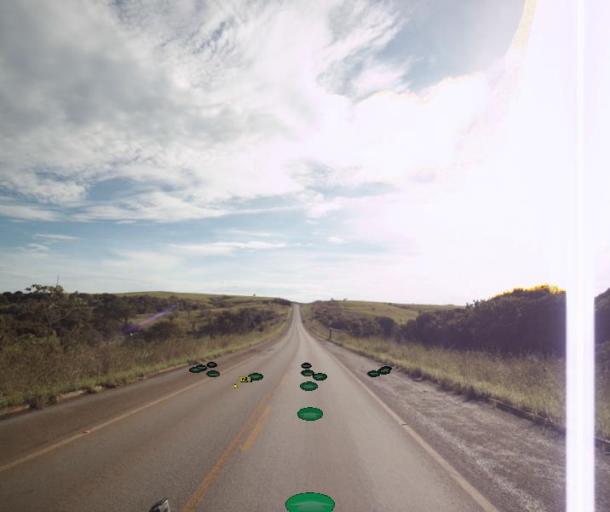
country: BR
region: Goias
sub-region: Abadiania
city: Abadiania
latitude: -15.7818
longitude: -48.4732
